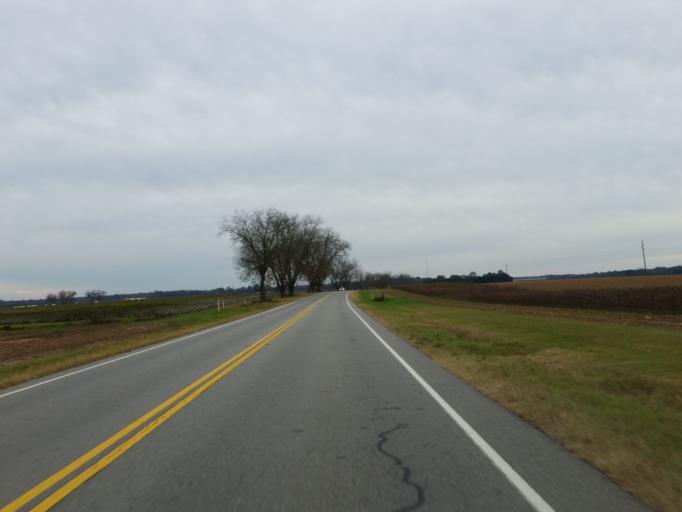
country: US
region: Georgia
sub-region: Dooly County
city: Vienna
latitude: 32.1696
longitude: -83.7701
